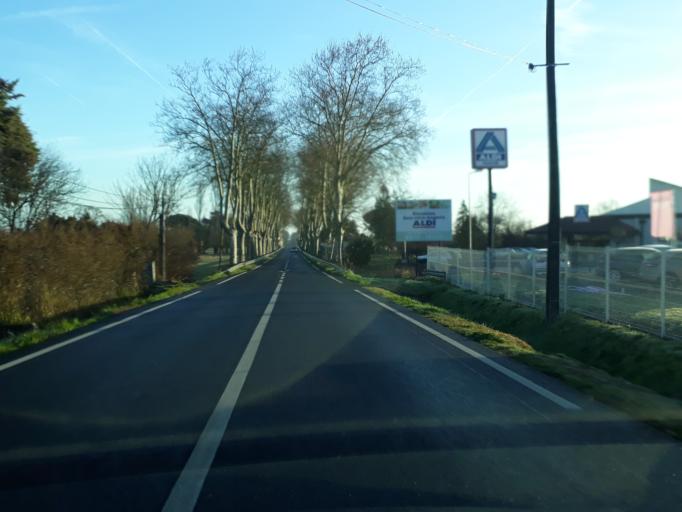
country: FR
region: Midi-Pyrenees
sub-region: Departement de la Haute-Garonne
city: Rieumes
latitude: 43.4140
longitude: 1.1275
